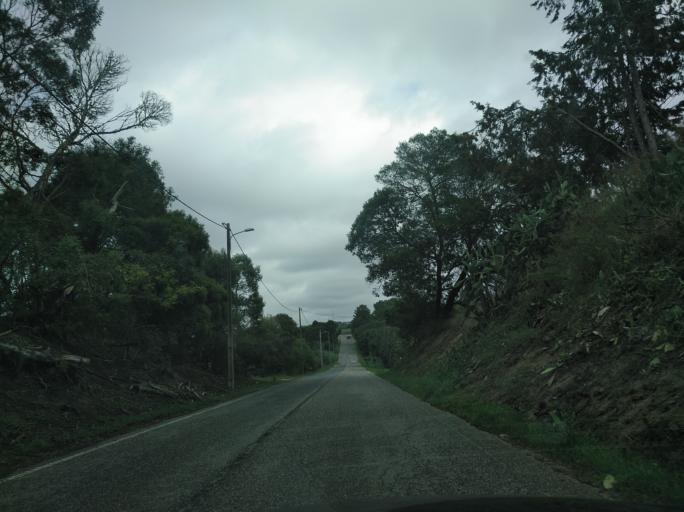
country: PT
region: Setubal
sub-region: Santiago do Cacem
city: Santo Andre
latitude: 38.1388
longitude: -8.7463
